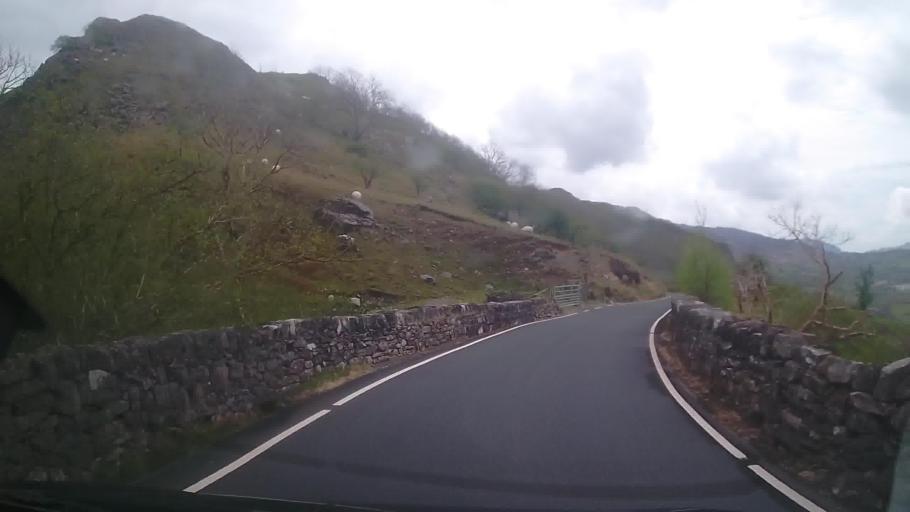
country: GB
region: Wales
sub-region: Gwynedd
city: Blaenau-Ffestiniog
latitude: 53.0646
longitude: -4.0014
